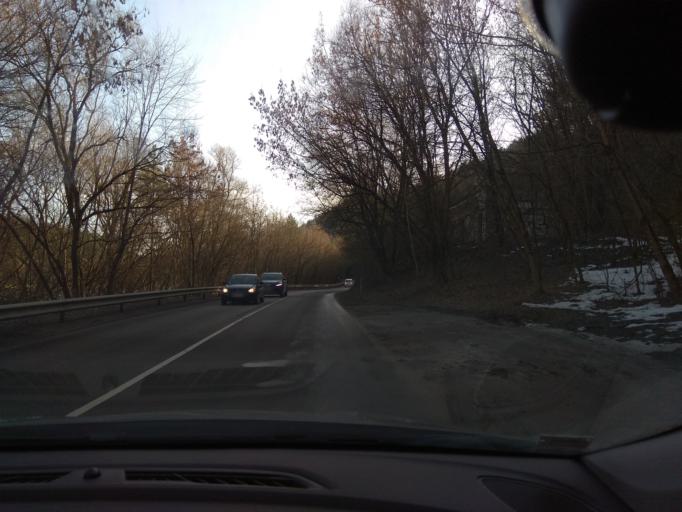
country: LT
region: Vilnius County
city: Lazdynai
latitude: 54.6615
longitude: 25.1740
